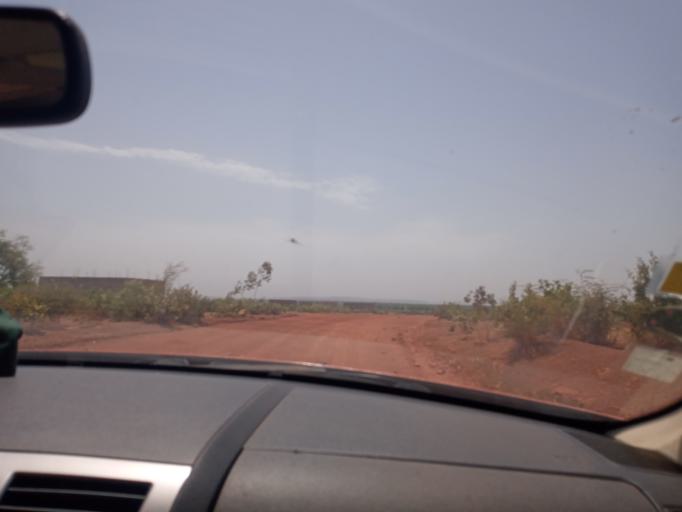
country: ML
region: Bamako
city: Bamako
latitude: 12.5163
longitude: -7.7907
